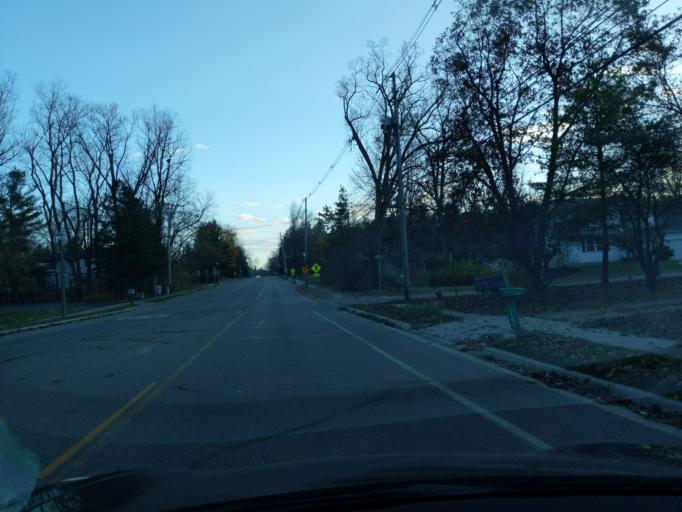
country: US
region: Michigan
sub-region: Ingham County
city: East Lansing
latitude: 42.7523
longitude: -84.4936
